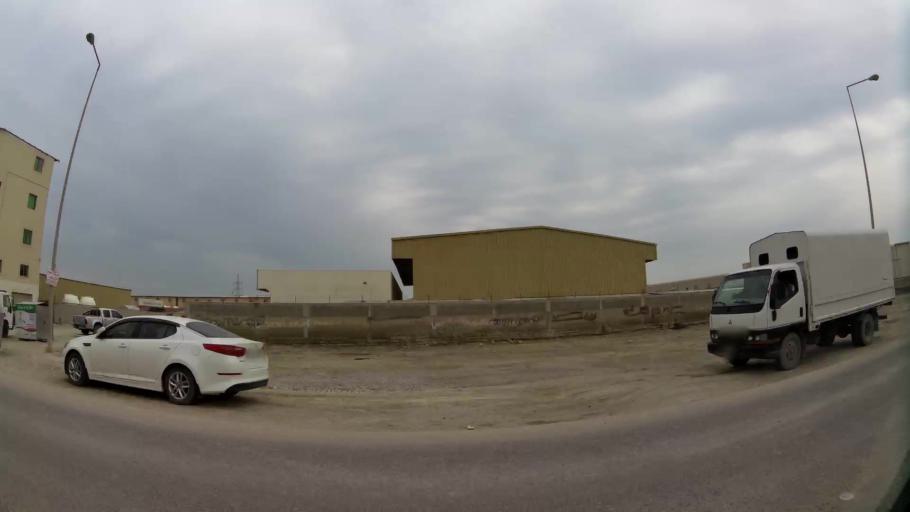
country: BH
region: Northern
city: Sitrah
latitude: 26.1758
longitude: 50.6097
